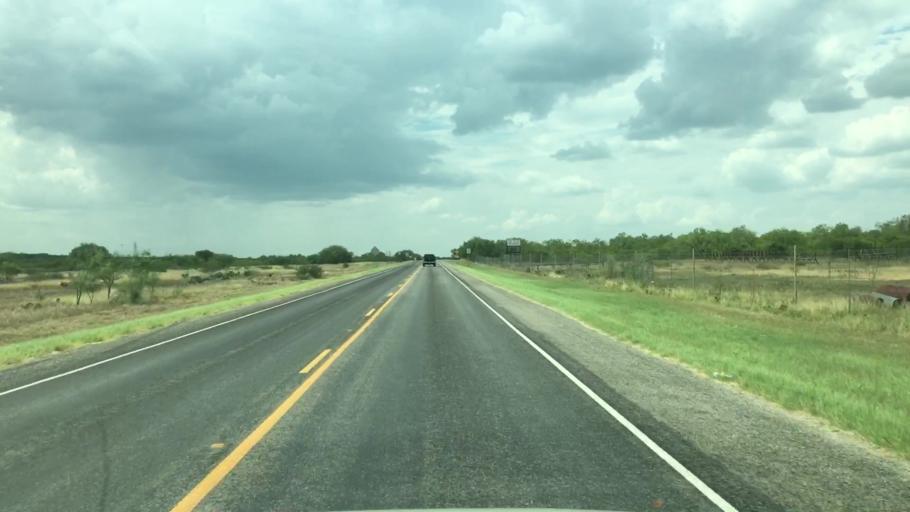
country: US
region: Texas
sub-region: Live Oak County
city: Three Rivers
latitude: 28.6375
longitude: -98.2772
